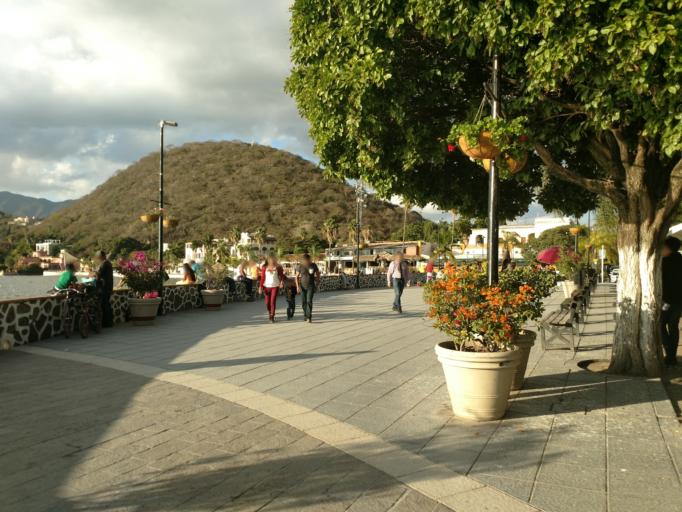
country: MX
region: Jalisco
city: Chapala
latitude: 20.2877
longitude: -103.1935
